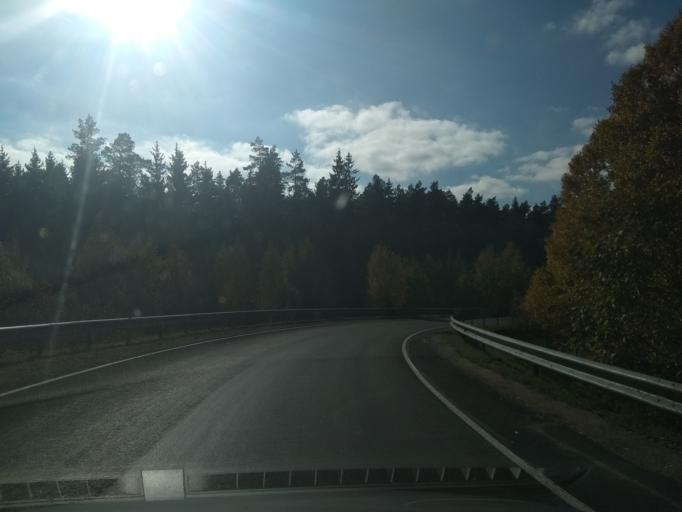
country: BY
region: Brest
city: Baranovichi
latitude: 53.0473
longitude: 25.8452
